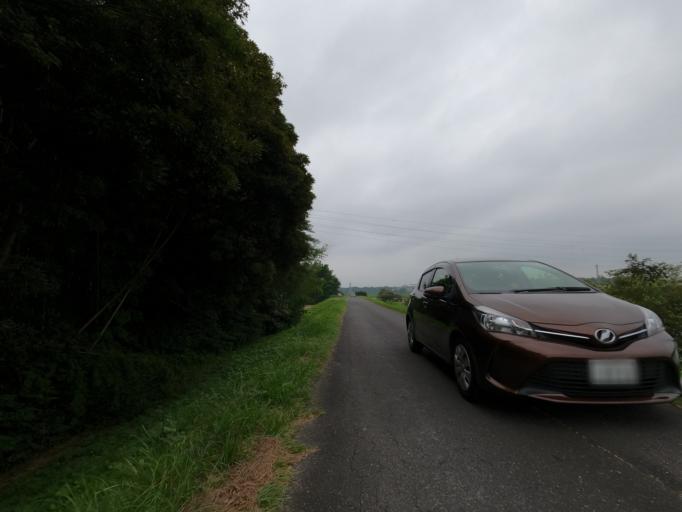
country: JP
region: Ibaraki
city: Moriya
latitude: 35.9435
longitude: 140.0293
